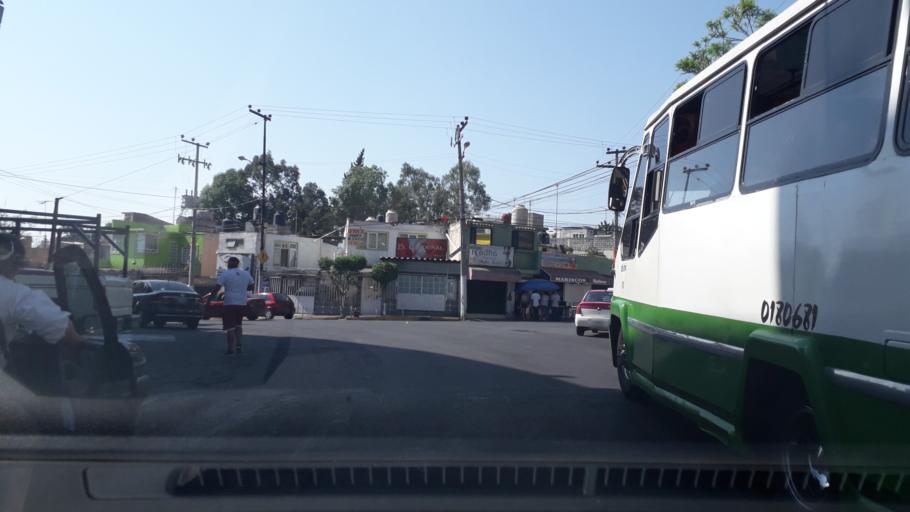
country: MX
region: Mexico City
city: Gustavo A. Madero
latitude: 19.5091
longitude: -99.1003
